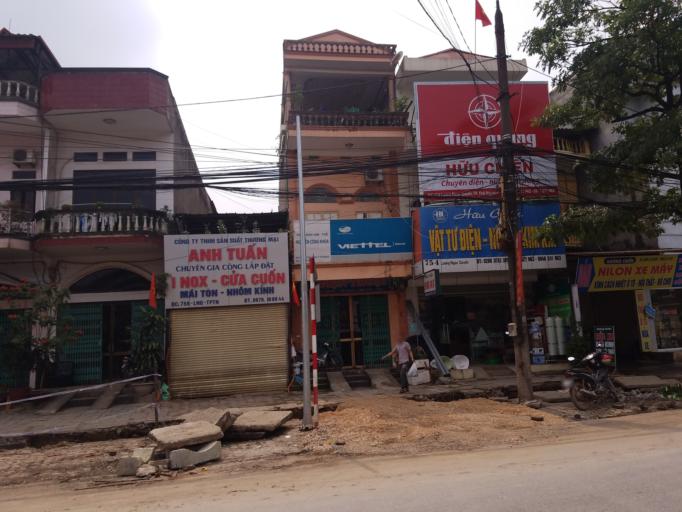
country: VN
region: Thai Nguyen
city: Thanh Pho Thai Nguyen
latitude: 21.5796
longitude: 105.8385
